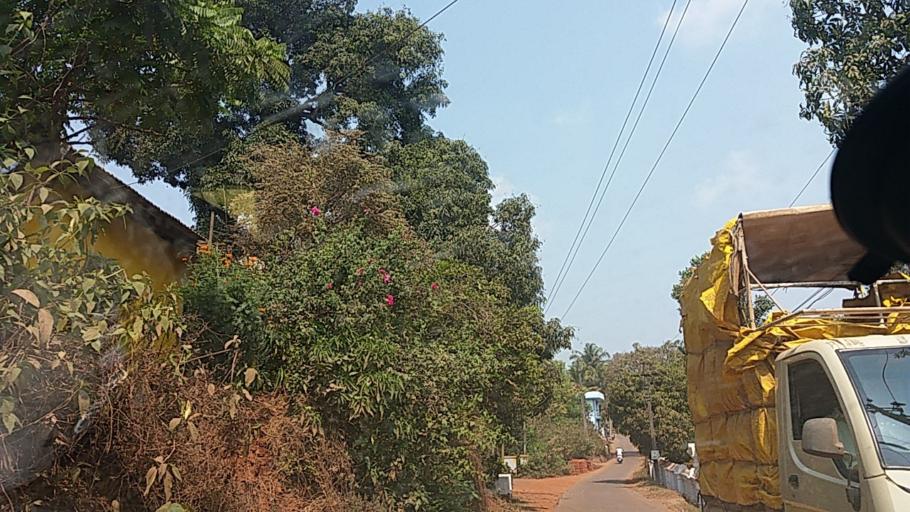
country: IN
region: Goa
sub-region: South Goa
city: Sancoale
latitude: 15.3702
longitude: 73.9154
